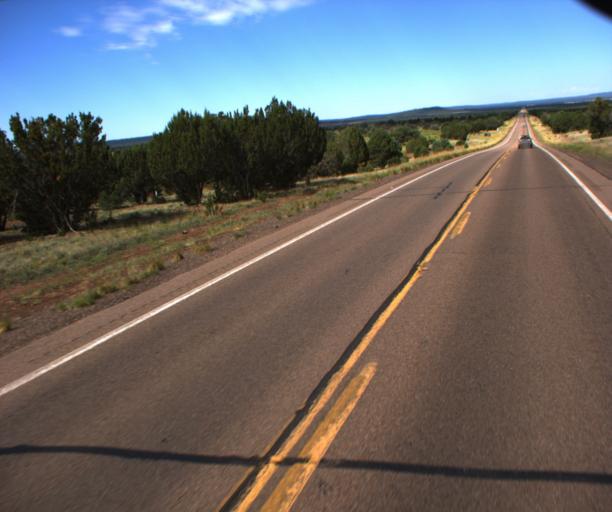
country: US
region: Arizona
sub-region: Navajo County
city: White Mountain Lake
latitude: 34.2749
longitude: -109.9004
